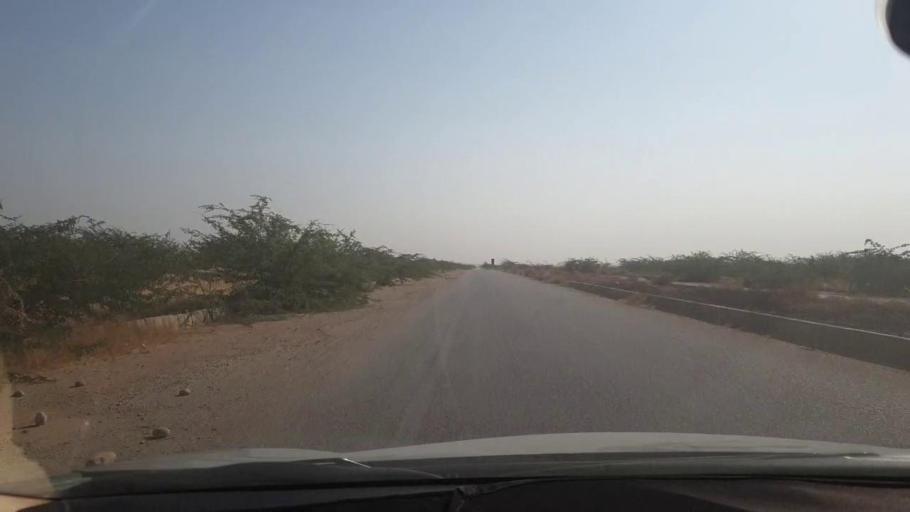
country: PK
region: Sindh
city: Malir Cantonment
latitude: 25.0745
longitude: 67.1385
